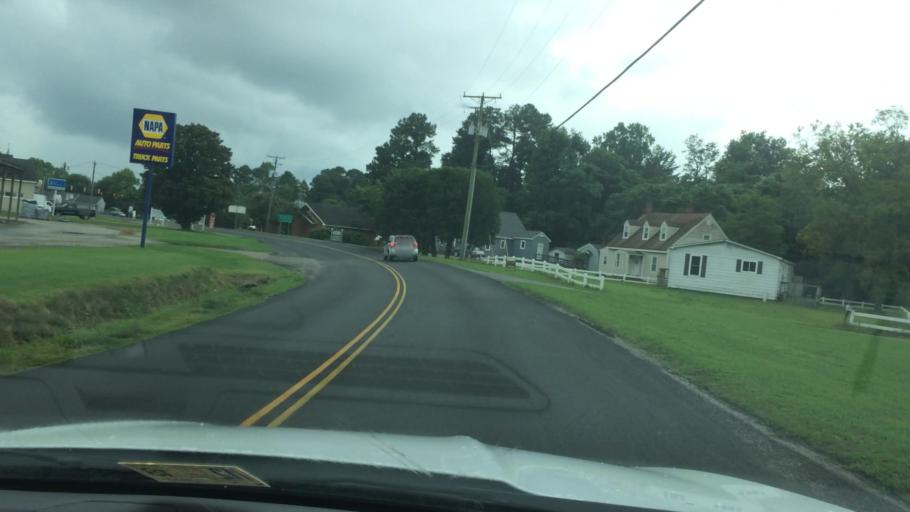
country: US
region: Virginia
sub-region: New Kent County
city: New Kent
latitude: 37.4445
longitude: -77.0444
